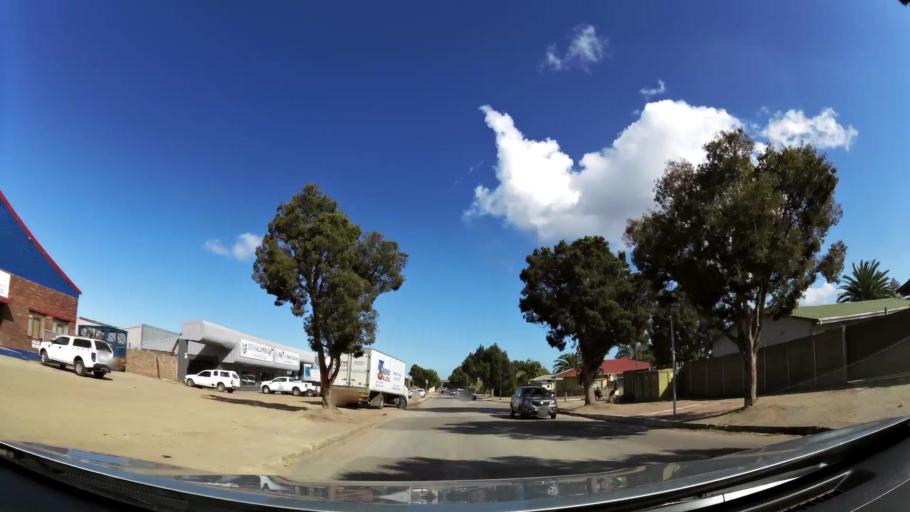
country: ZA
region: Western Cape
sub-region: Eden District Municipality
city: George
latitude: -33.9675
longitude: 22.4651
